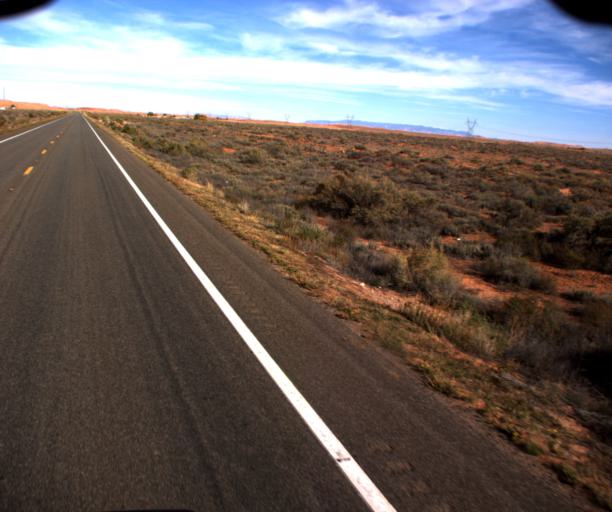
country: US
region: Arizona
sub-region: Navajo County
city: Kayenta
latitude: 36.8107
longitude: -109.9004
